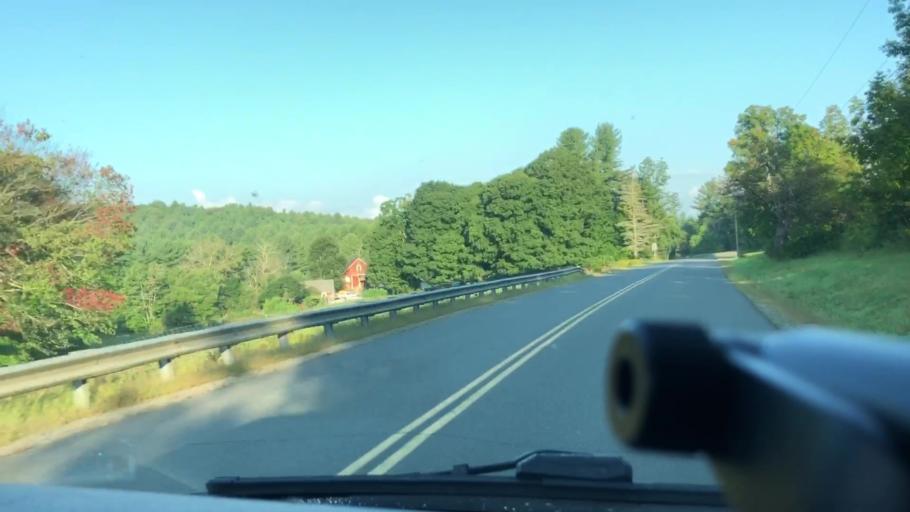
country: US
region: Massachusetts
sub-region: Franklin County
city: Ashfield
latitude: 42.4968
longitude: -72.8686
